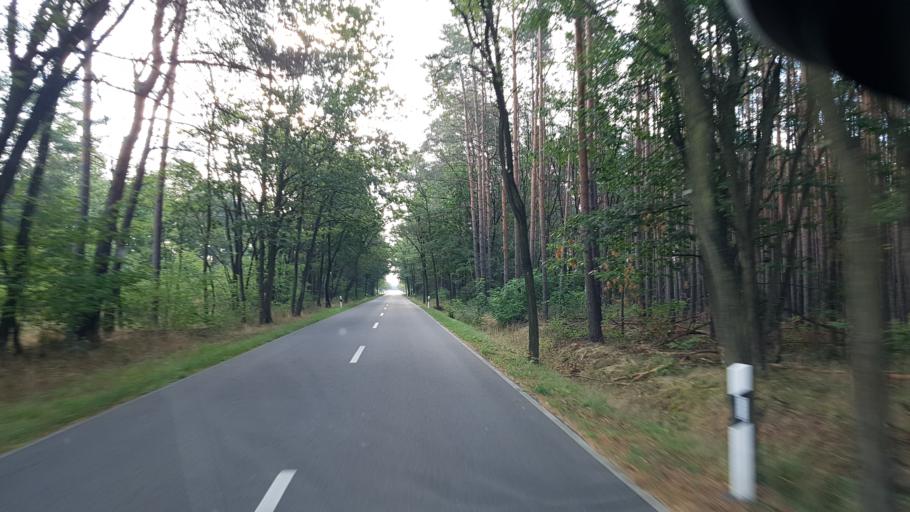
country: DE
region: Brandenburg
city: Welzow
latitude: 51.5550
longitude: 14.1656
